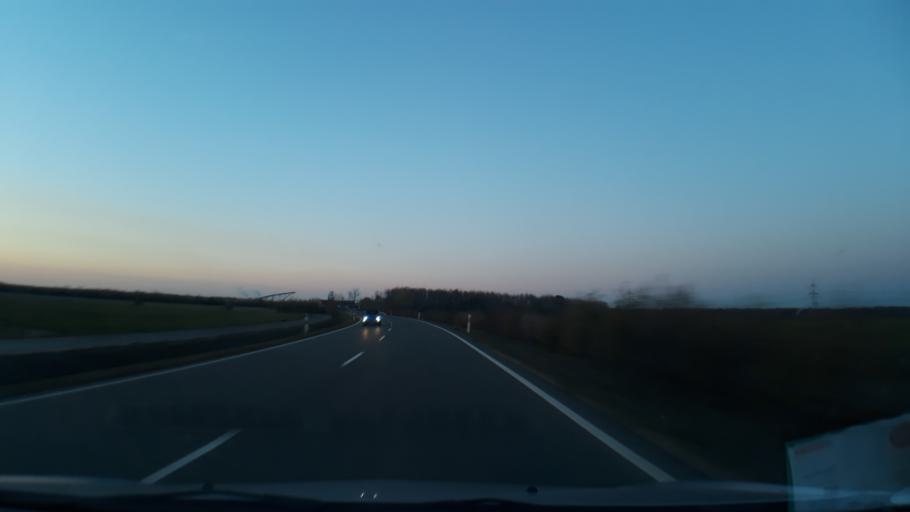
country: DE
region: North Rhine-Westphalia
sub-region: Regierungsbezirk Koln
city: Kerpen
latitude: 50.8709
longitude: 6.6376
